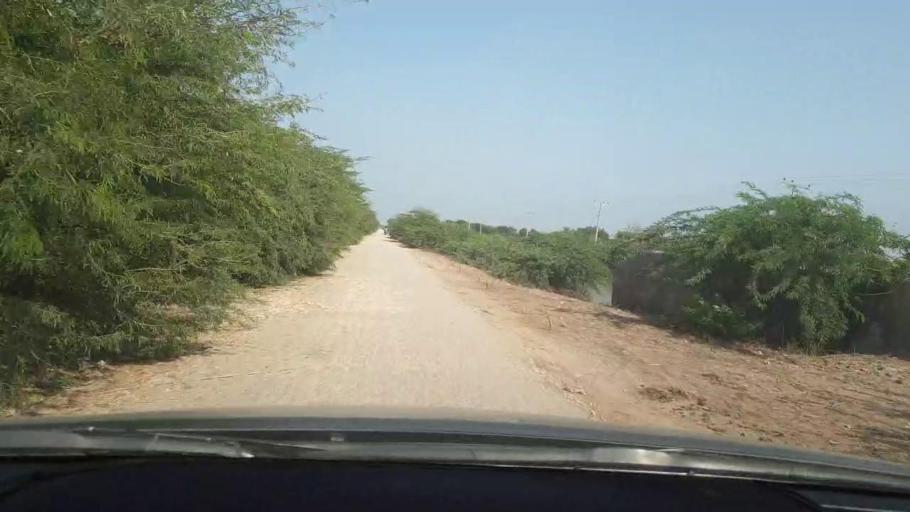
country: PK
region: Sindh
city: Naukot
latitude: 24.7610
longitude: 69.2093
